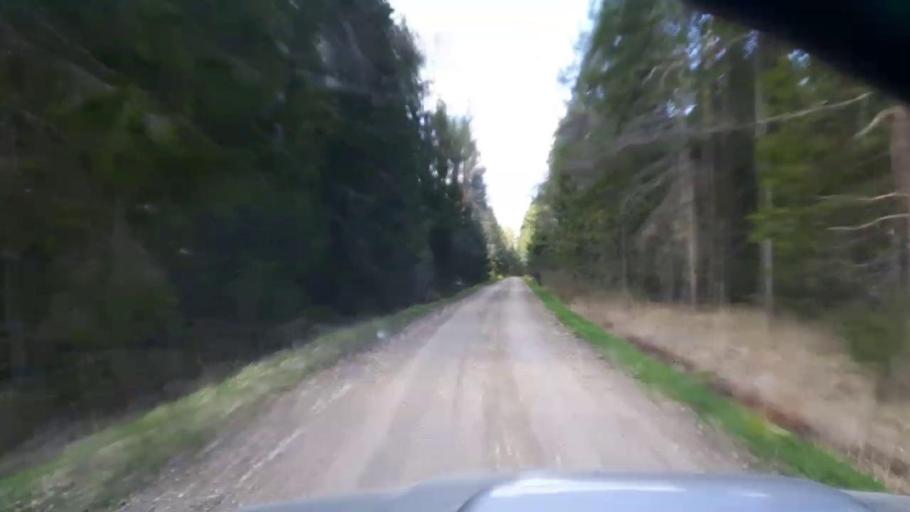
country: EE
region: Paernumaa
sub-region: Tootsi vald
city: Tootsi
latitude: 58.4434
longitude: 24.9343
